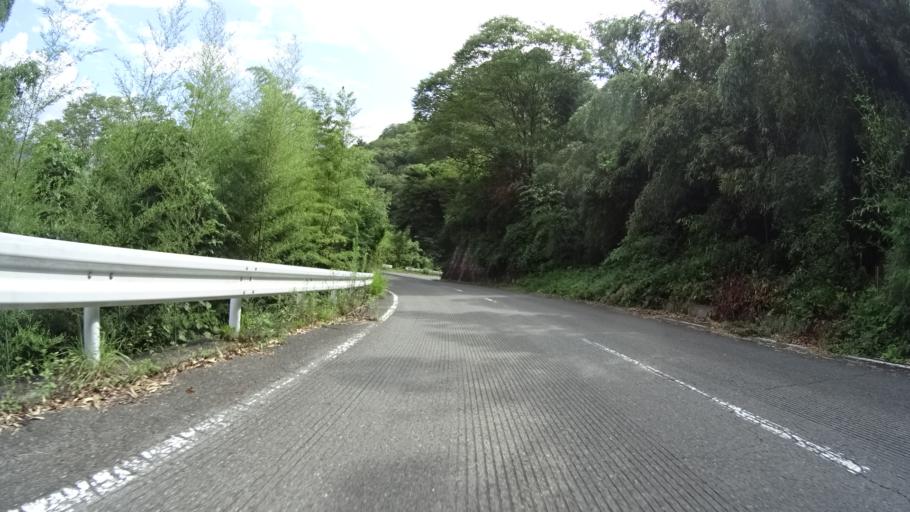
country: JP
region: Yamanashi
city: Kofu-shi
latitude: 35.7683
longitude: 138.5557
